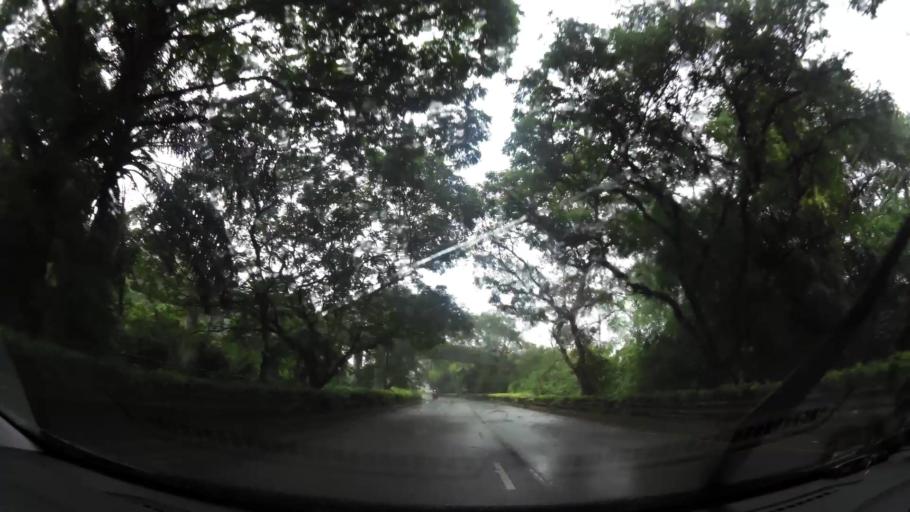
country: MY
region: Johor
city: Kampung Pasir Gudang Baru
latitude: 1.3936
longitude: 103.8333
